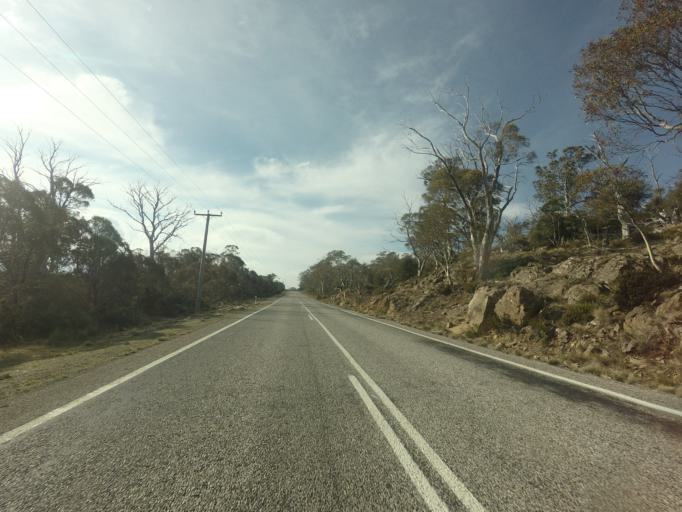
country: AU
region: Tasmania
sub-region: Meander Valley
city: Deloraine
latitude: -41.9912
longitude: 146.7083
